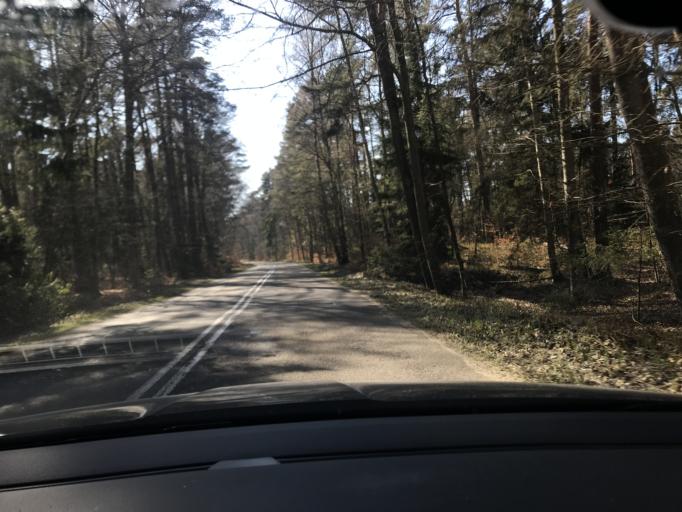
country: PL
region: Pomeranian Voivodeship
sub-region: Powiat nowodworski
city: Krynica Morska
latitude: 54.3606
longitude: 19.3499
